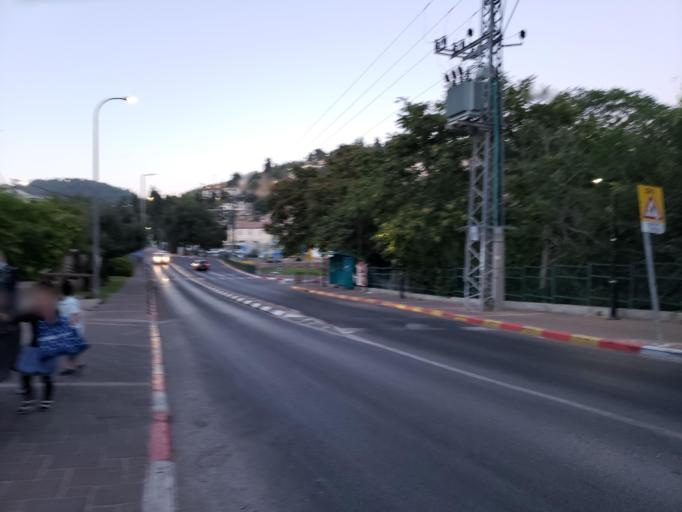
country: IL
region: Northern District
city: Safed
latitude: 32.9669
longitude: 35.4970
